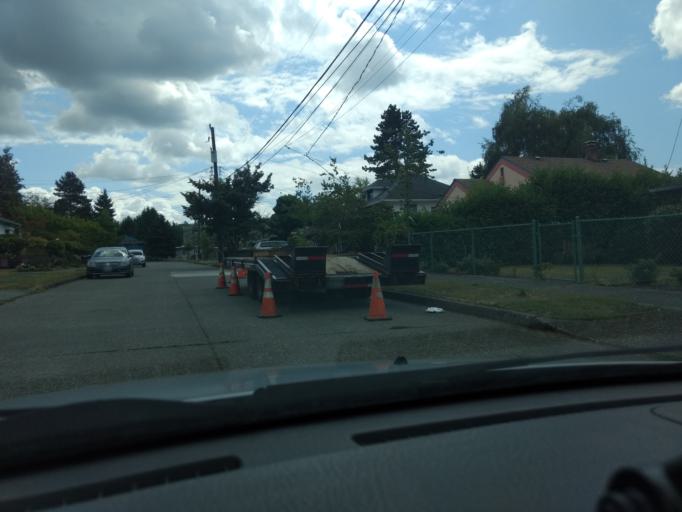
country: US
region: Washington
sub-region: King County
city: Bryn Mawr-Skyway
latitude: 47.5179
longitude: -122.2663
